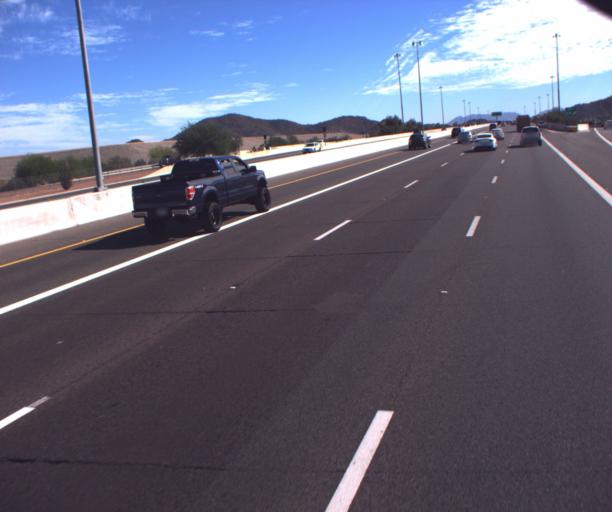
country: US
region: Arizona
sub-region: Maricopa County
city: Glendale
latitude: 33.6687
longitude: -112.0723
